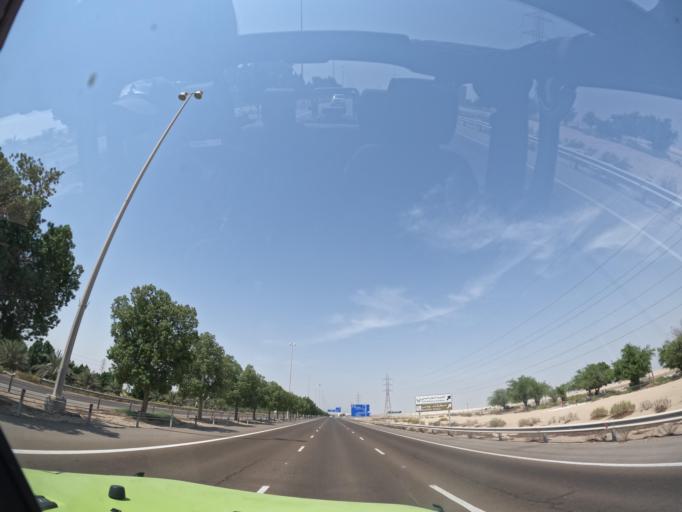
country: AE
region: Abu Dhabi
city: Abu Dhabi
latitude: 24.2209
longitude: 54.8332
